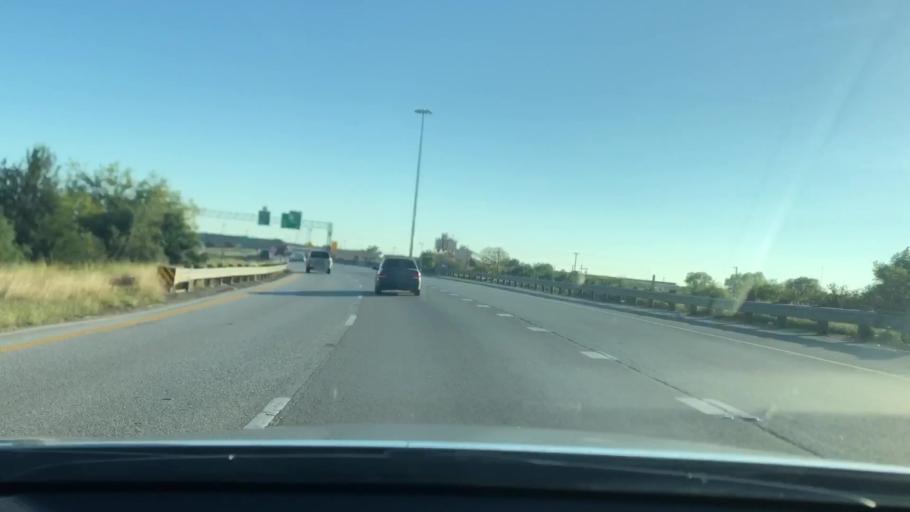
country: US
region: Texas
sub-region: Bexar County
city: Kirby
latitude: 29.4529
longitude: -98.4059
